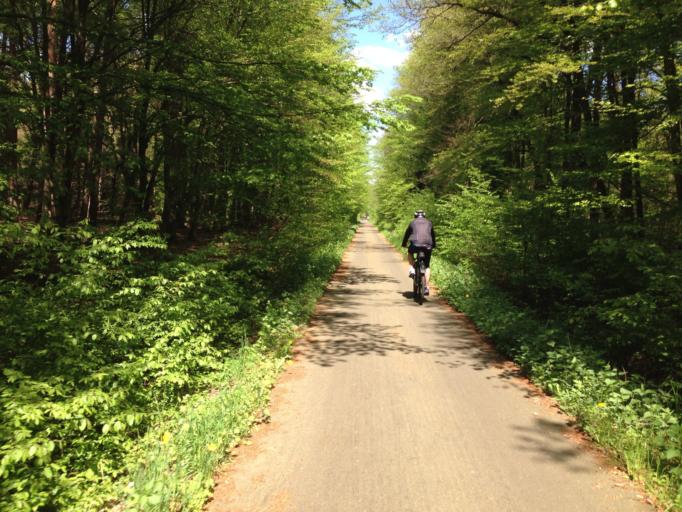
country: DE
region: Hesse
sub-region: Regierungsbezirk Giessen
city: Hungen
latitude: 50.4961
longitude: 8.9070
